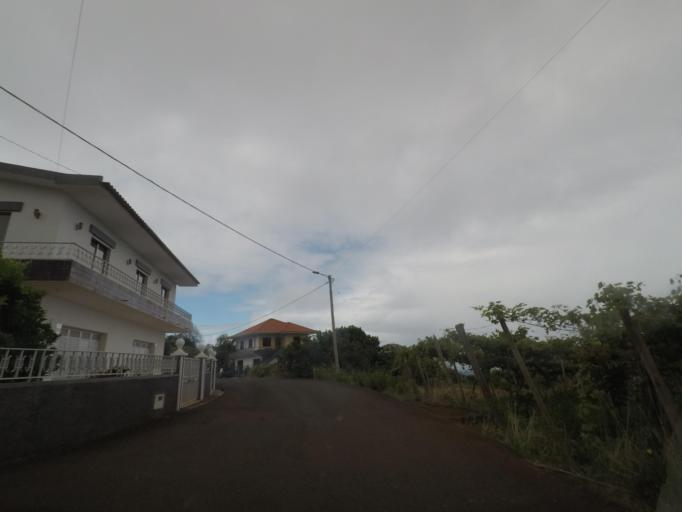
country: PT
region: Madeira
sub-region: Santana
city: Santana
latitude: 32.8310
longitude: -16.9128
